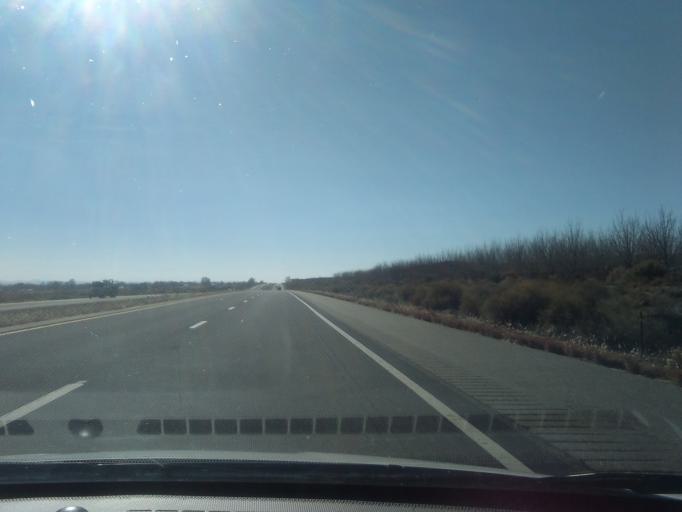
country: US
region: New Mexico
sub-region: Valencia County
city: Jarales
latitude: 34.5949
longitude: -106.7889
